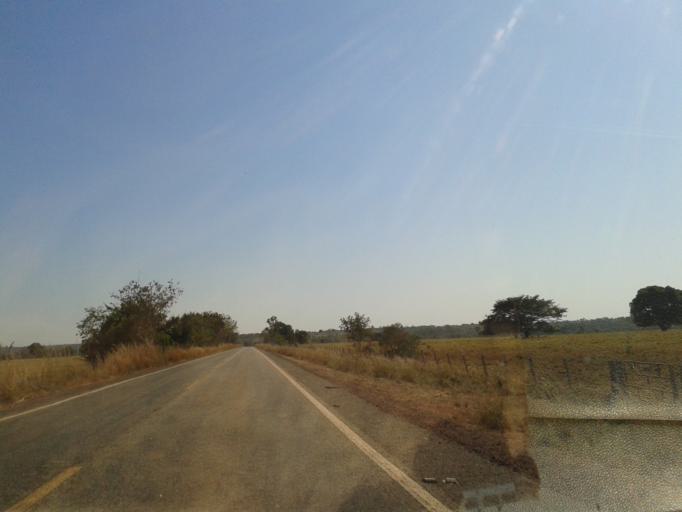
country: BR
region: Goias
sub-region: Mozarlandia
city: Mozarlandia
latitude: -14.5018
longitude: -50.4847
